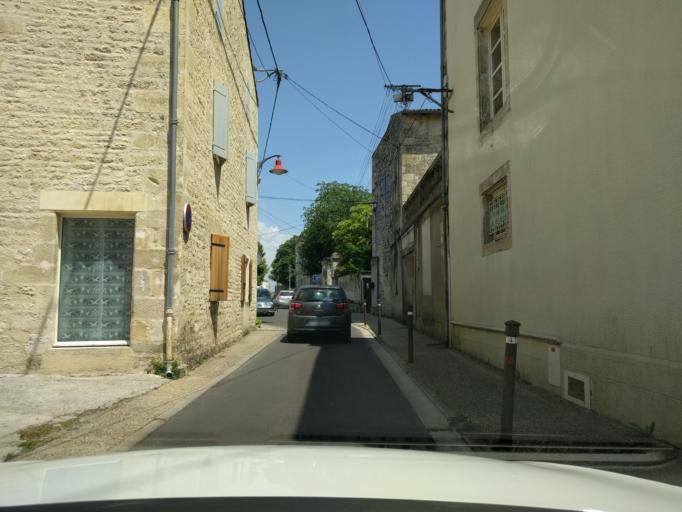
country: FR
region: Poitou-Charentes
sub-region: Departement des Deux-Sevres
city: Niort
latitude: 46.3481
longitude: -0.4707
